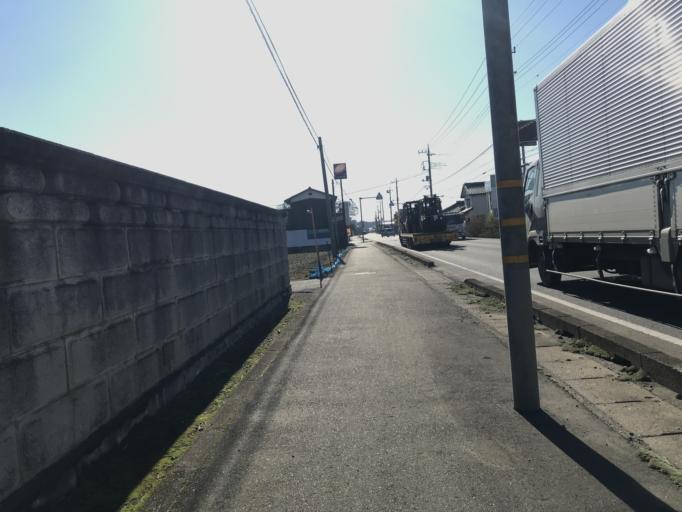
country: JP
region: Ibaraki
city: Sakai
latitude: 36.1623
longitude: 139.8097
